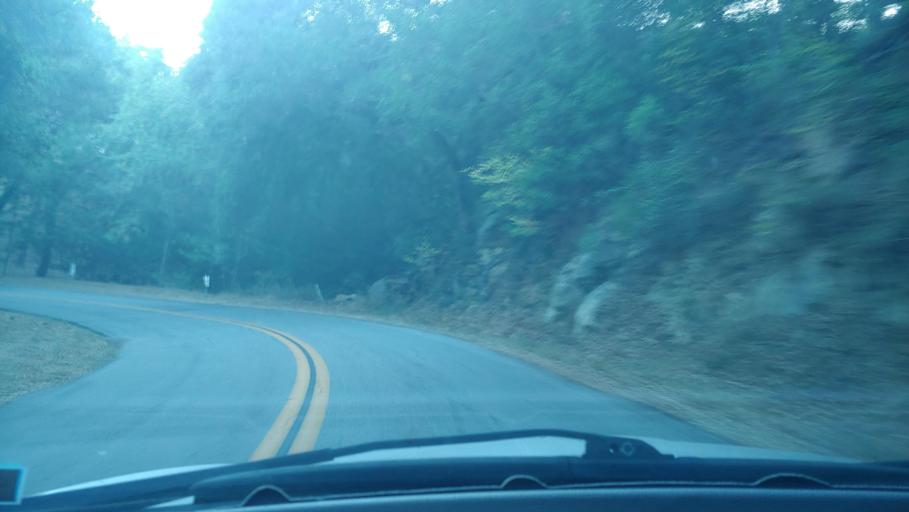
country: US
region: California
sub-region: Santa Barbara County
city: Goleta
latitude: 34.5172
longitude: -119.8301
